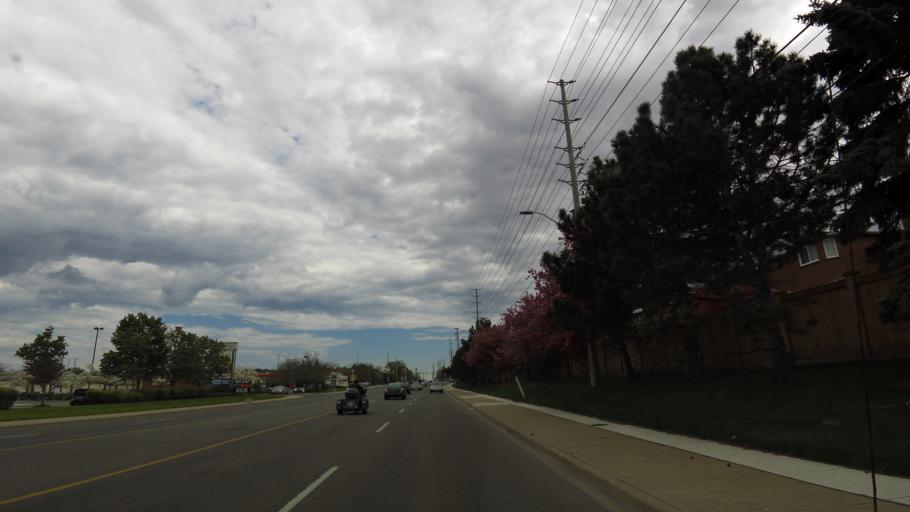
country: CA
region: Ontario
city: Mississauga
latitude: 43.5990
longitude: -79.7140
